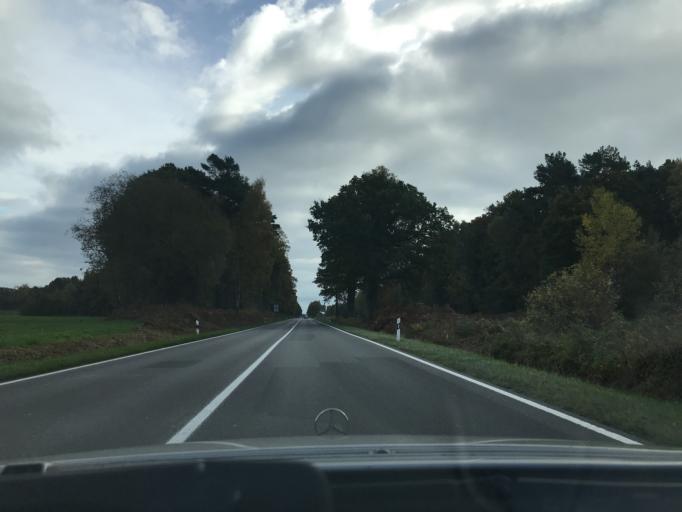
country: DE
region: Mecklenburg-Vorpommern
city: Koserow
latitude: 54.0619
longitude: 13.9820
